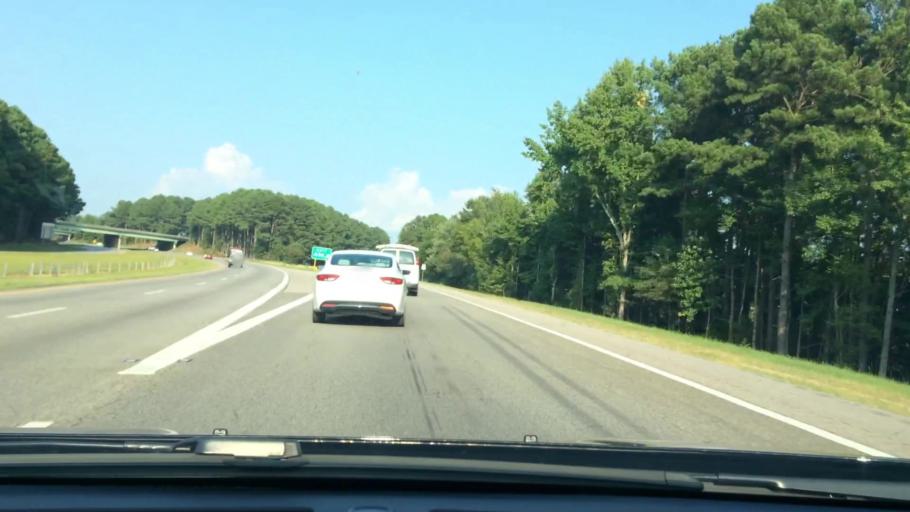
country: US
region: North Carolina
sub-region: Wake County
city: Zebulon
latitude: 35.8346
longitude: -78.3081
